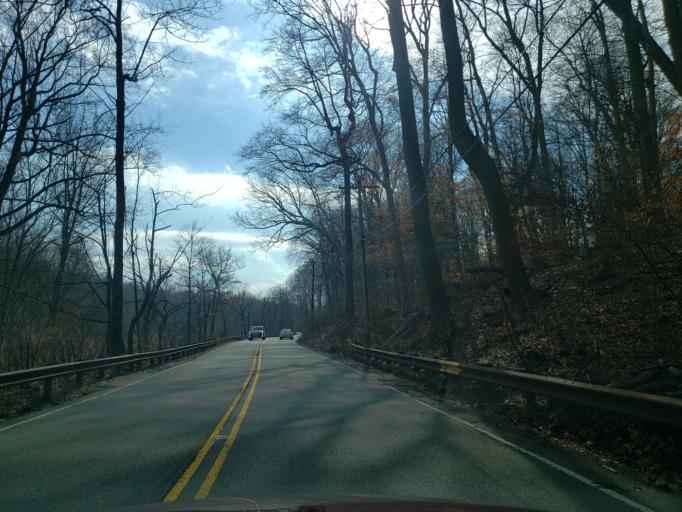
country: US
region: New Jersey
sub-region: Essex County
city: Short Hills
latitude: 40.7339
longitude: -74.3078
